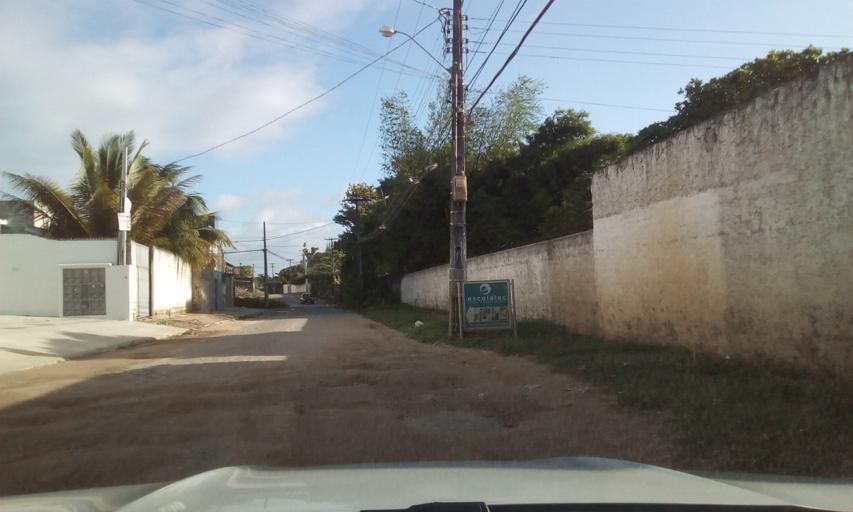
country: BR
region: Paraiba
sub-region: Joao Pessoa
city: Joao Pessoa
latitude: -7.1600
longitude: -34.8509
